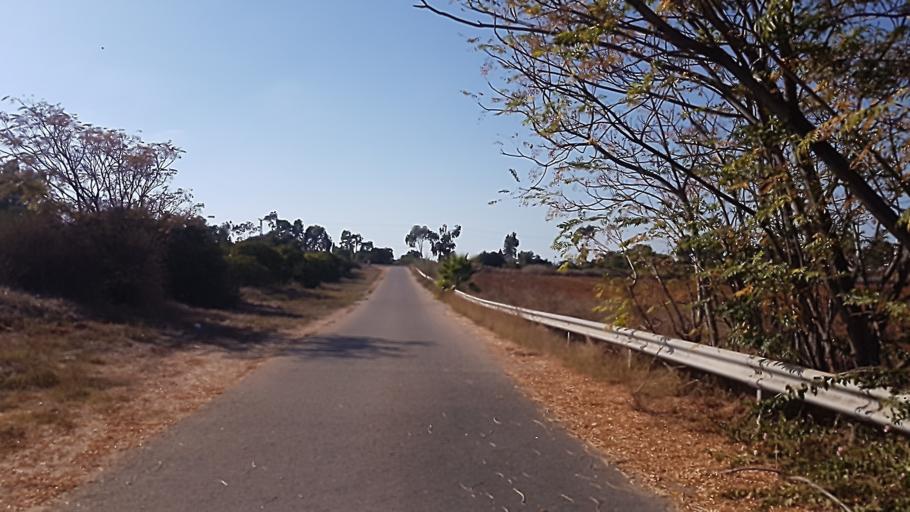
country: IL
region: Central District
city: Kfar Saba
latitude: 32.2018
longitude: 34.9164
